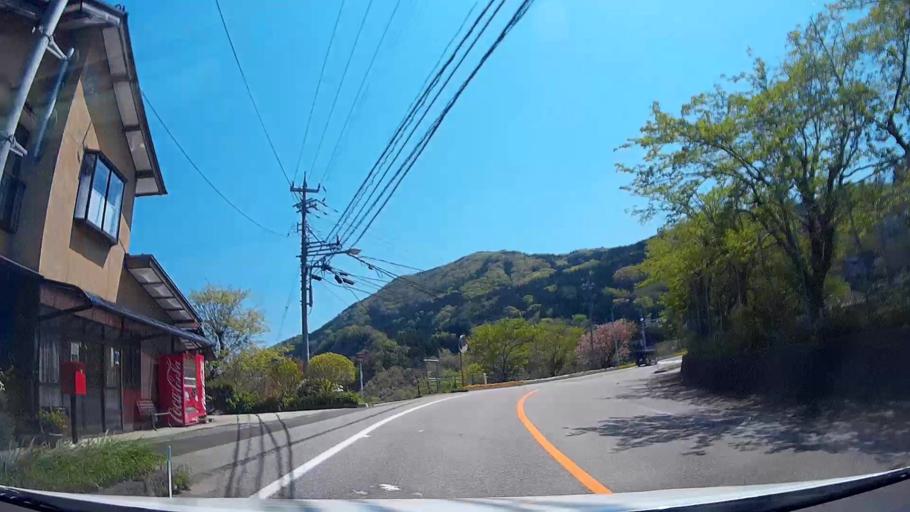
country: JP
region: Ishikawa
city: Nanao
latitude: 37.4112
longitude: 136.9695
